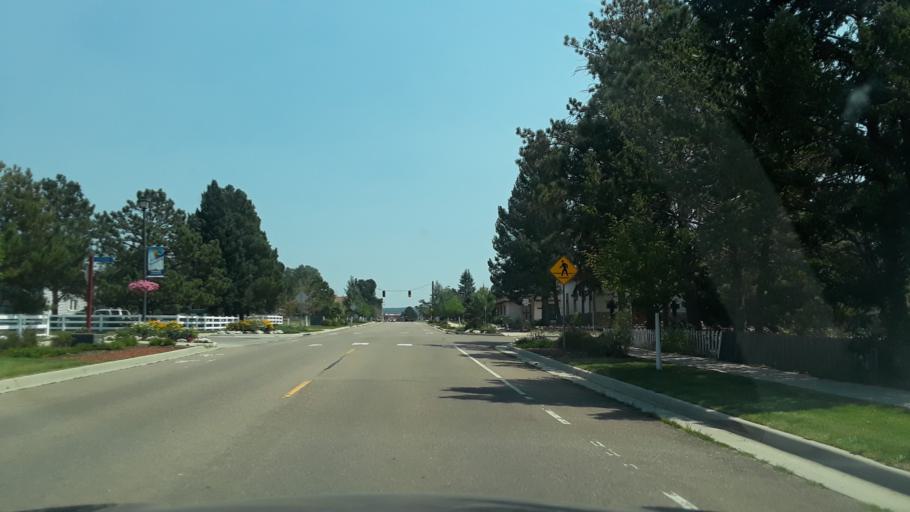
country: US
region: Colorado
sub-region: El Paso County
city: Monument
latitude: 39.0931
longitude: -104.8718
